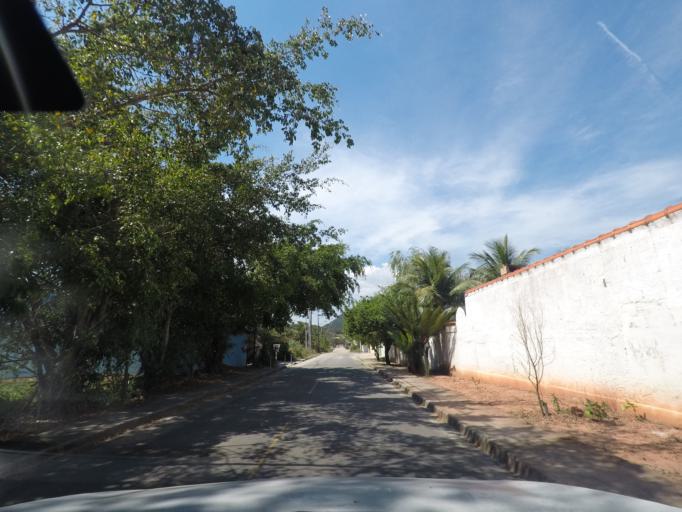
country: BR
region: Rio de Janeiro
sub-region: Marica
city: Marica
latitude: -22.9602
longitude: -42.9676
